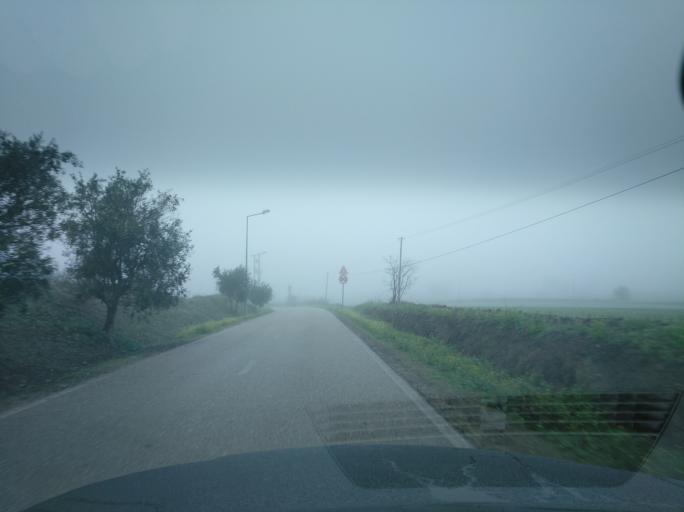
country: PT
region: Portalegre
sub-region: Campo Maior
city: Campo Maior
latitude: 39.0242
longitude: -7.0680
